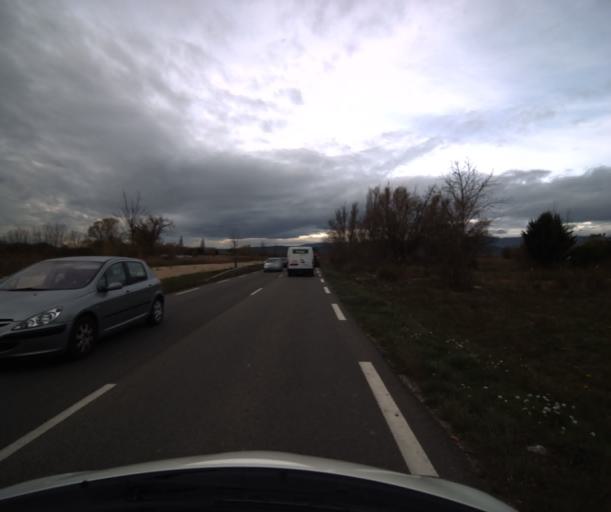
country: FR
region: Provence-Alpes-Cote d'Azur
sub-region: Departement du Vaucluse
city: Pertuis
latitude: 43.6743
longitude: 5.4929
